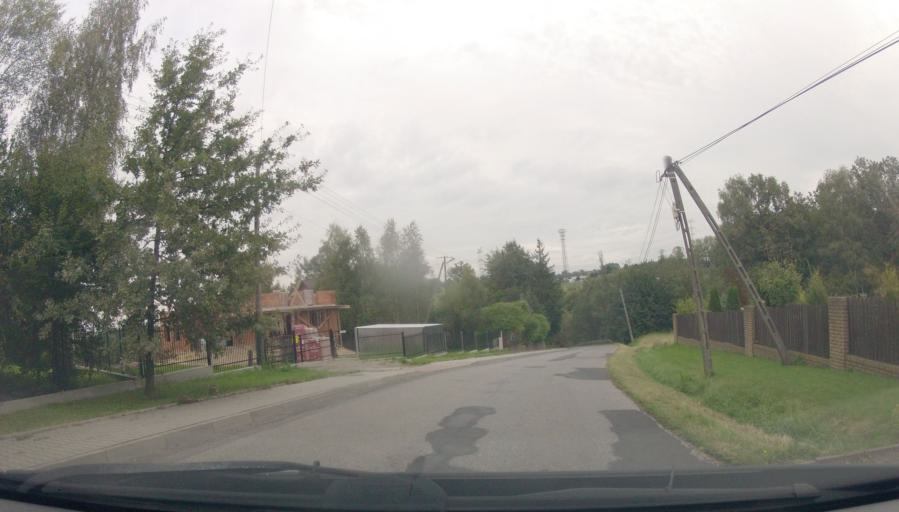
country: PL
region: Lesser Poland Voivodeship
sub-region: Powiat krakowski
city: Rzeszotary
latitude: 49.9425
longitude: 19.9923
